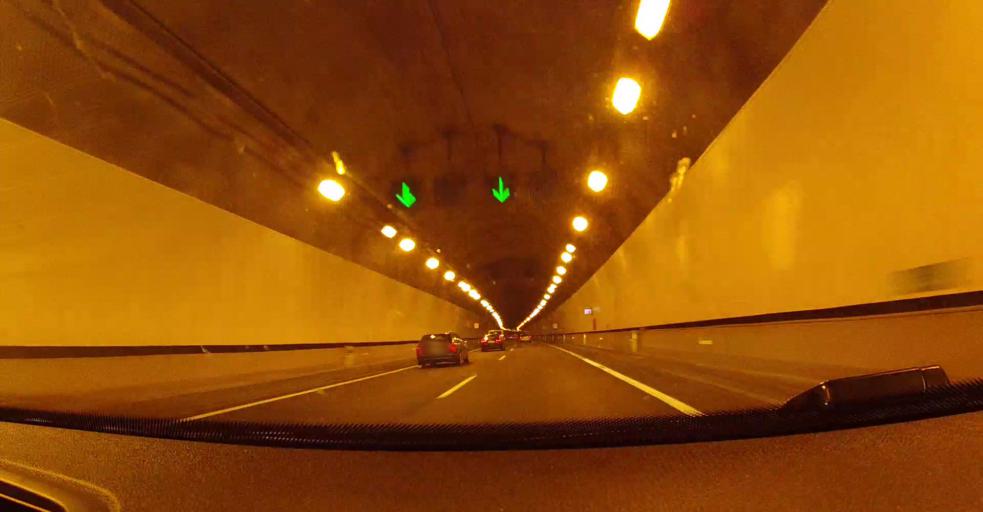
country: ES
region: Basque Country
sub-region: Provincia de Guipuzcoa
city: Bergara
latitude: 43.1452
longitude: -2.4282
